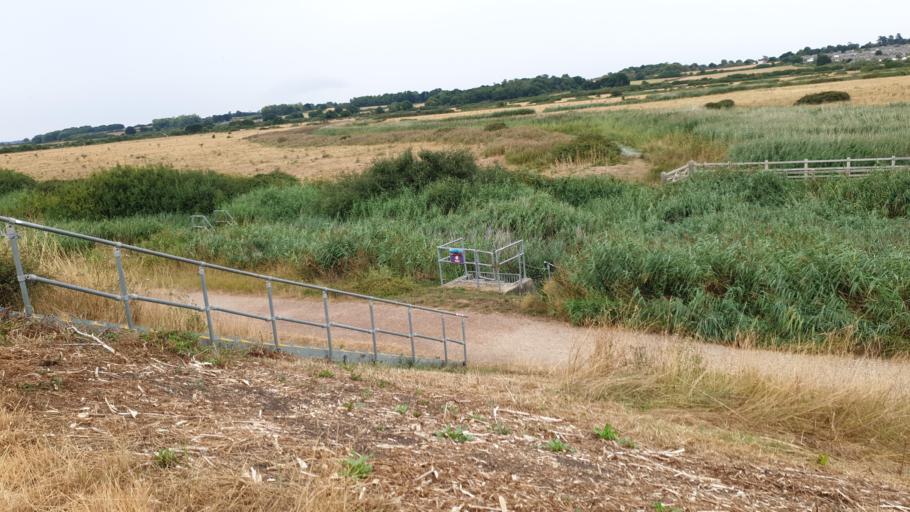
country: GB
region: England
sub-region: Essex
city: Brightlingsea
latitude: 51.8076
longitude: 1.0084
